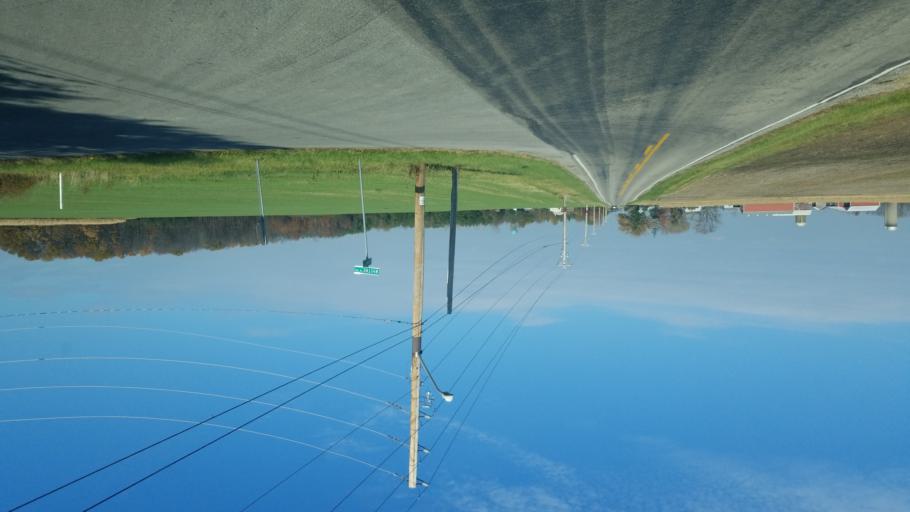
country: US
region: Ohio
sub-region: Lorain County
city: Camden
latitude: 41.2235
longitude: -82.2564
